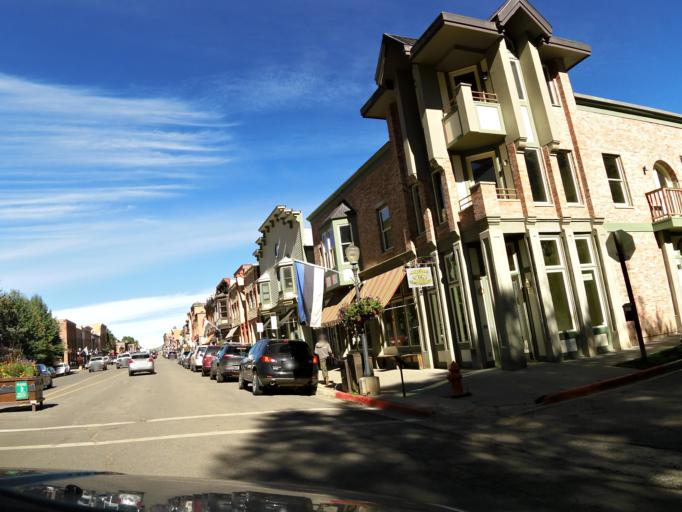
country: US
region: Colorado
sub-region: San Miguel County
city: Telluride
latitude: 37.9364
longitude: -107.8077
